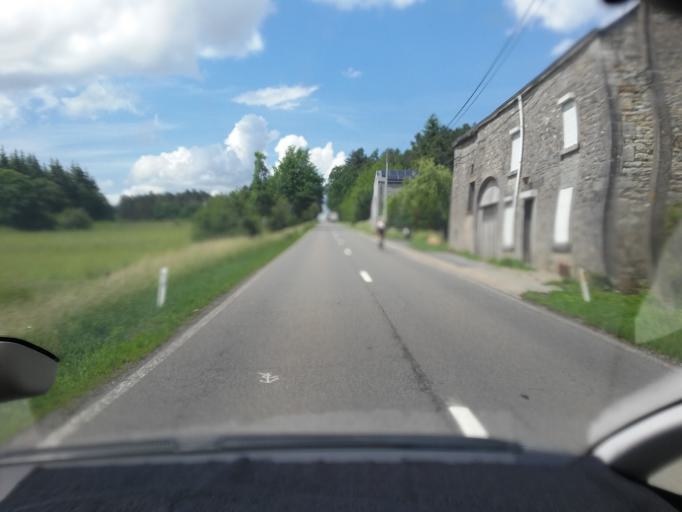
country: BE
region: Wallonia
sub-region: Province de Namur
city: Rochefort
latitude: 50.1307
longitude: 5.2358
